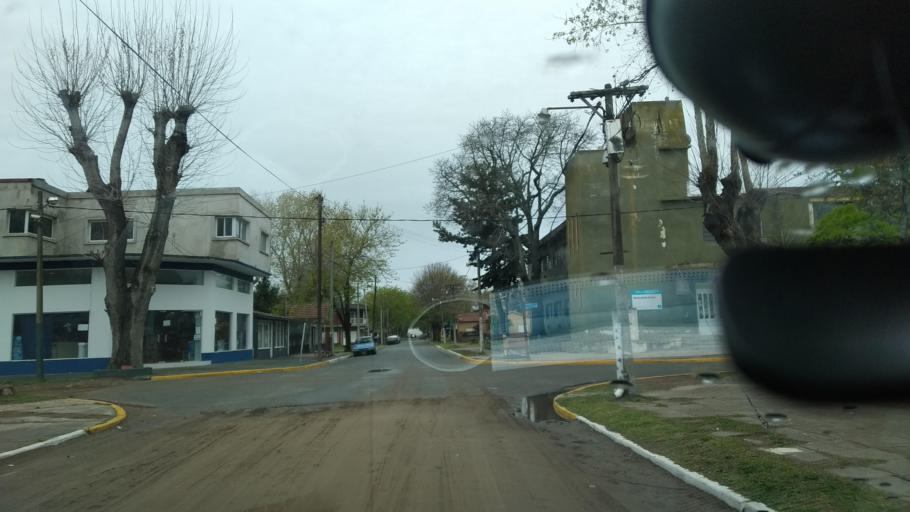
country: AR
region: Buenos Aires
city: Mar del Tuyu
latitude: -36.5306
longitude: -56.7124
